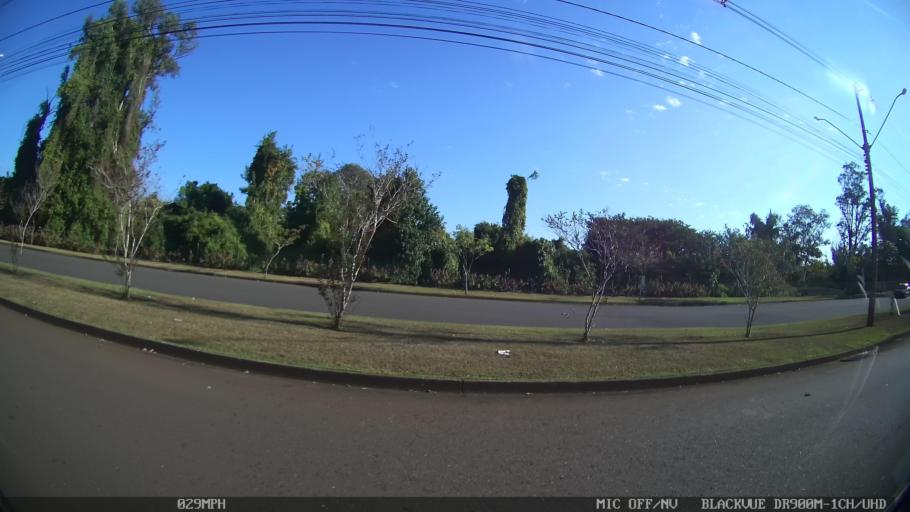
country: BR
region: Sao Paulo
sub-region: Piracicaba
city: Piracicaba
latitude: -22.6917
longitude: -47.6273
